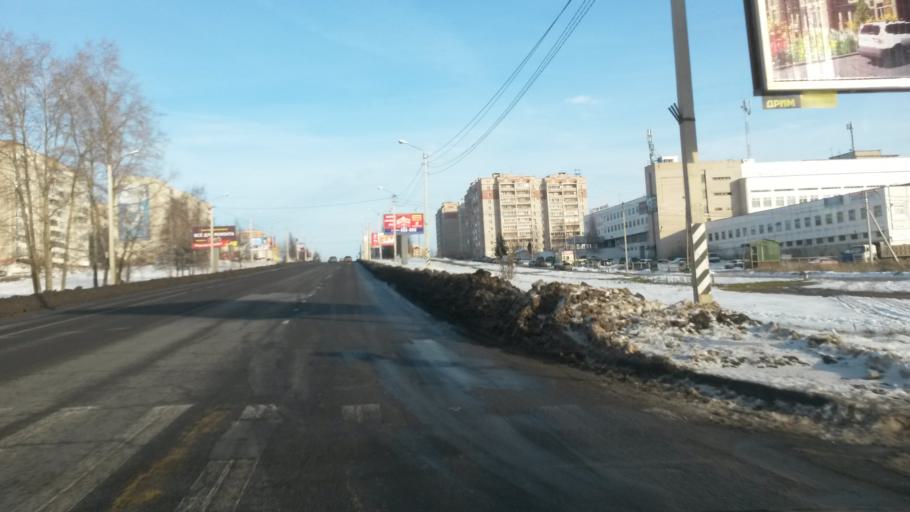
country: RU
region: Kostroma
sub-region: Kostromskoy Rayon
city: Kostroma
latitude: 57.7322
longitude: 40.9049
